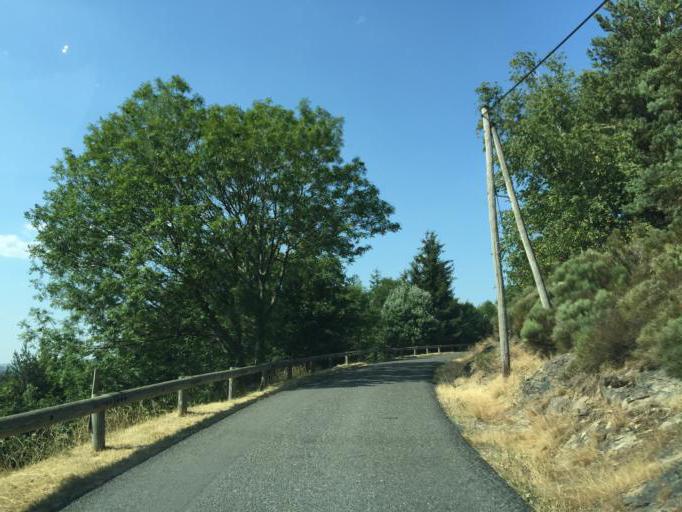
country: FR
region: Rhone-Alpes
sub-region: Departement de la Loire
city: Saint-Jean-Bonnefonds
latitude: 45.4328
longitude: 4.4581
